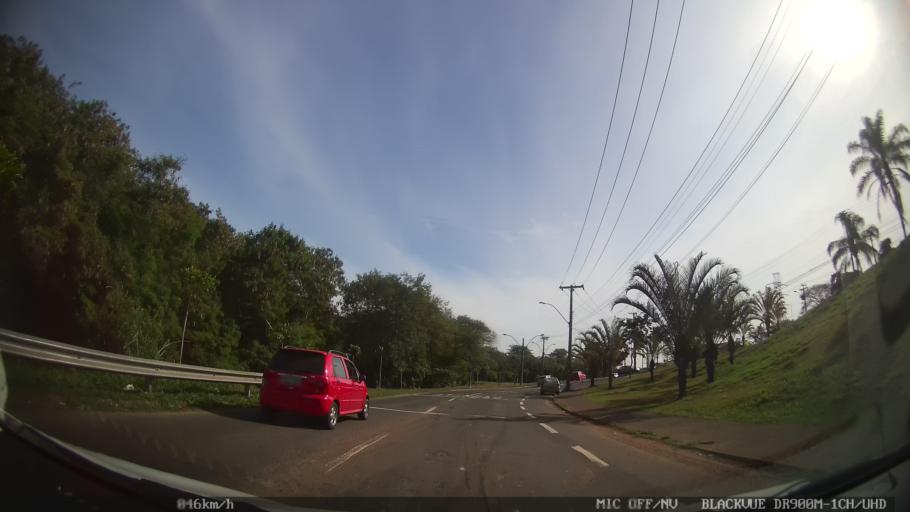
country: BR
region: Sao Paulo
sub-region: Piracicaba
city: Piracicaba
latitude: -22.7324
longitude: -47.6716
